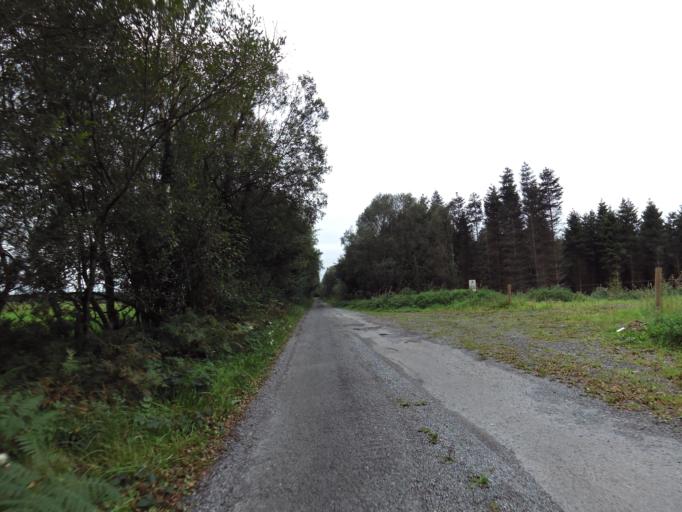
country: IE
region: Leinster
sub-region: Uibh Fhaili
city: Ferbane
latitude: 53.2455
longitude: -7.7408
